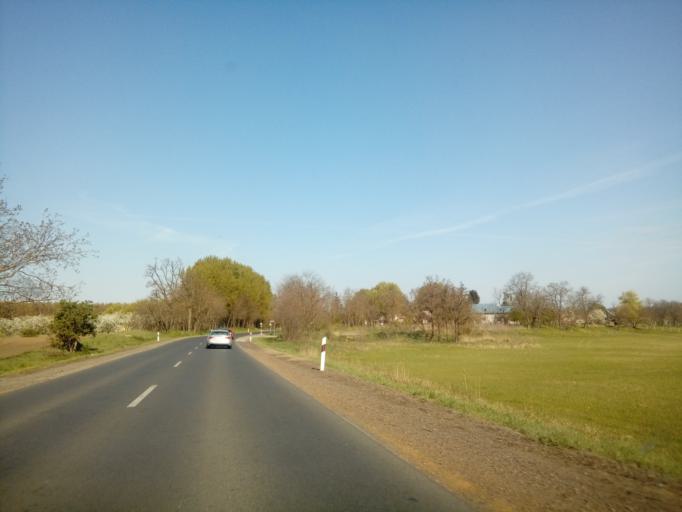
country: HU
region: Szabolcs-Szatmar-Bereg
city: Nagykallo
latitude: 47.8987
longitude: 21.7942
